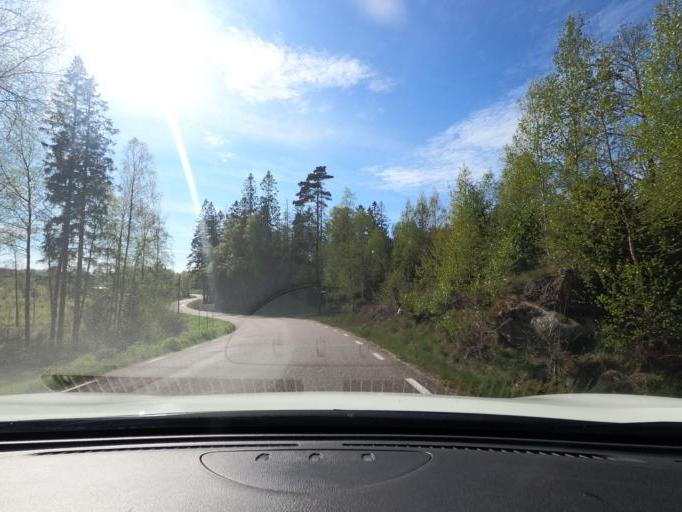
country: SE
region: Vaestra Goetaland
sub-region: Harryda Kommun
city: Landvetter
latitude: 57.6191
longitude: 12.3135
